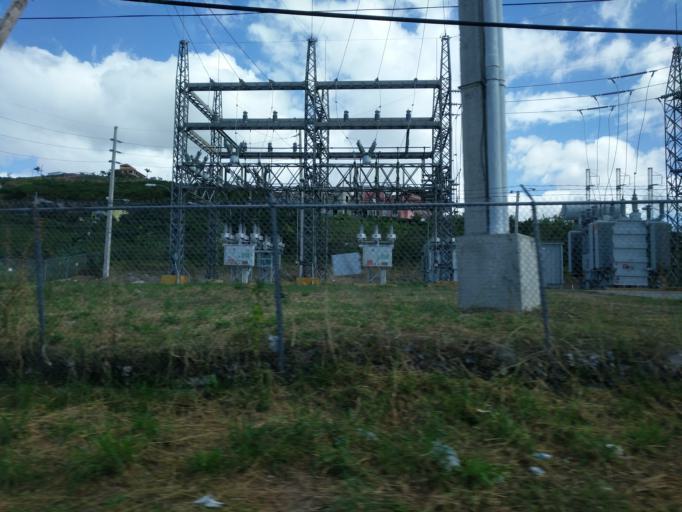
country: PR
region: Santa Isabel Municipio
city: El Ojo
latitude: 18.0222
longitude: -66.3700
